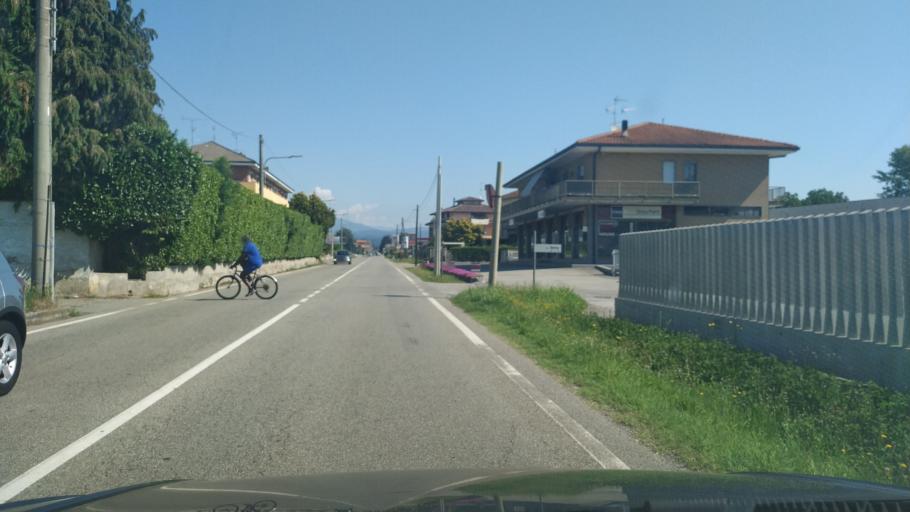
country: IT
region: Piedmont
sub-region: Provincia di Novara
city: Cureggio
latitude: 45.6796
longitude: 8.4563
